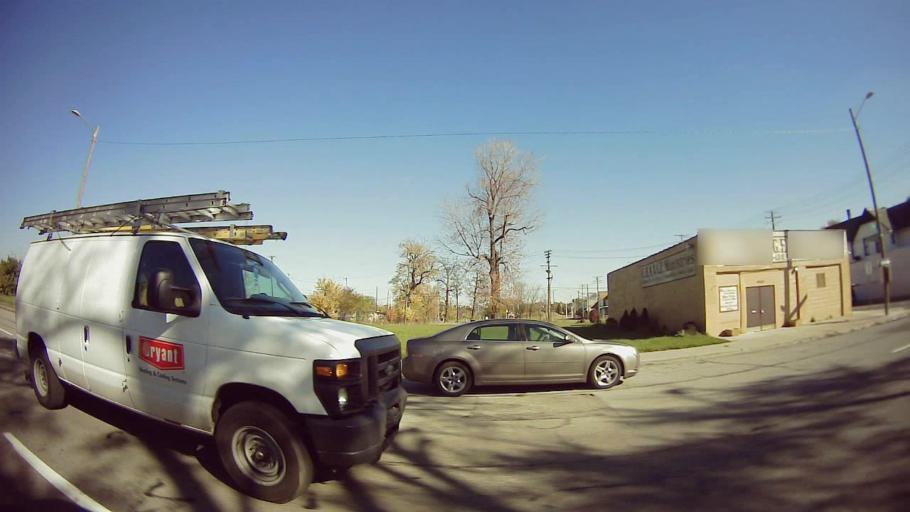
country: US
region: Michigan
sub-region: Wayne County
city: Detroit
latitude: 42.3454
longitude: -83.0846
